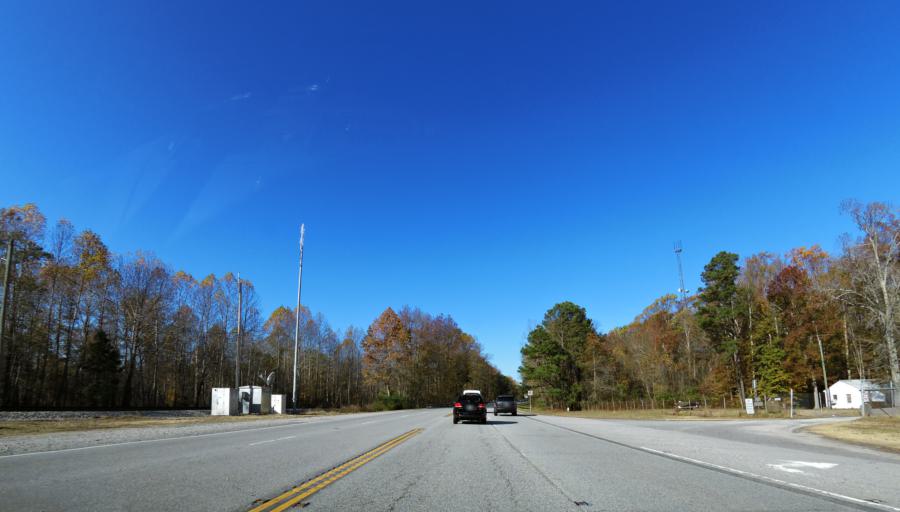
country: US
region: Virginia
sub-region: York County
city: Yorktown
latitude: 37.2140
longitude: -76.5994
